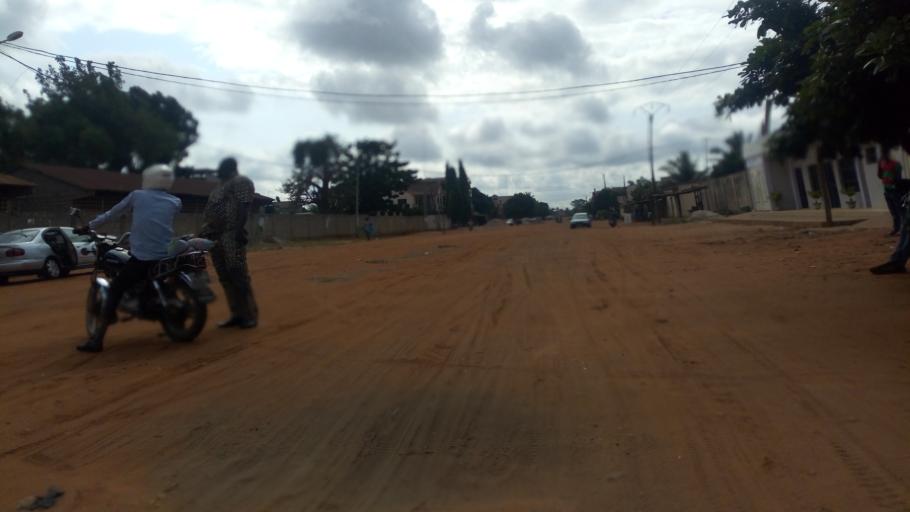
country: TG
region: Maritime
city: Lome
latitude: 6.2190
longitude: 1.1912
